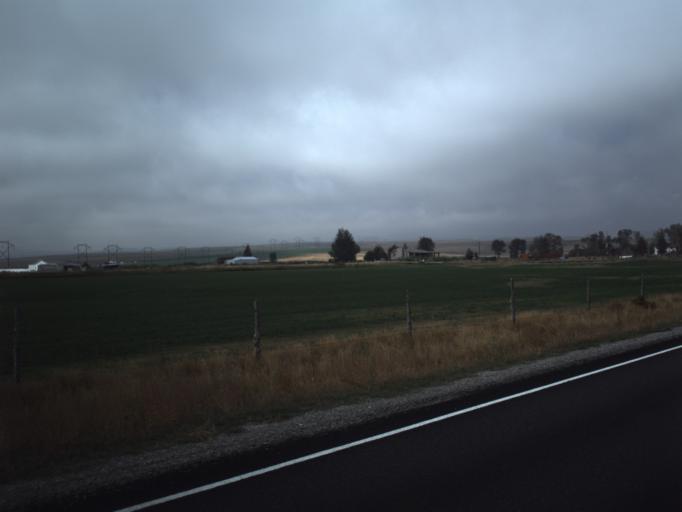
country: US
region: Utah
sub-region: Rich County
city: Randolph
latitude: 41.5174
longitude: -111.1572
